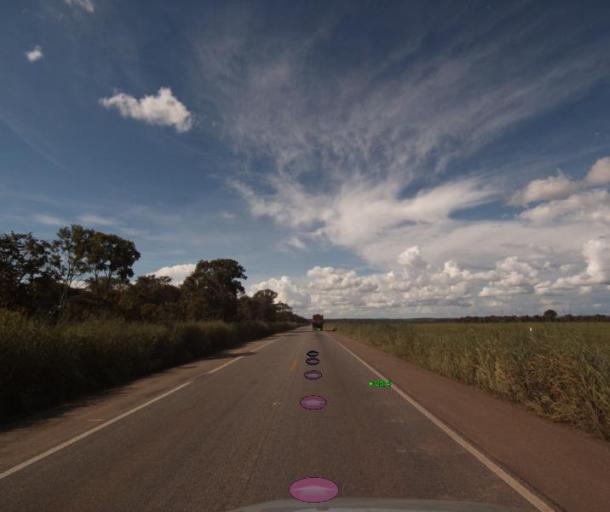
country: BR
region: Goias
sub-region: Porangatu
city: Porangatu
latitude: -13.0507
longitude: -49.1774
